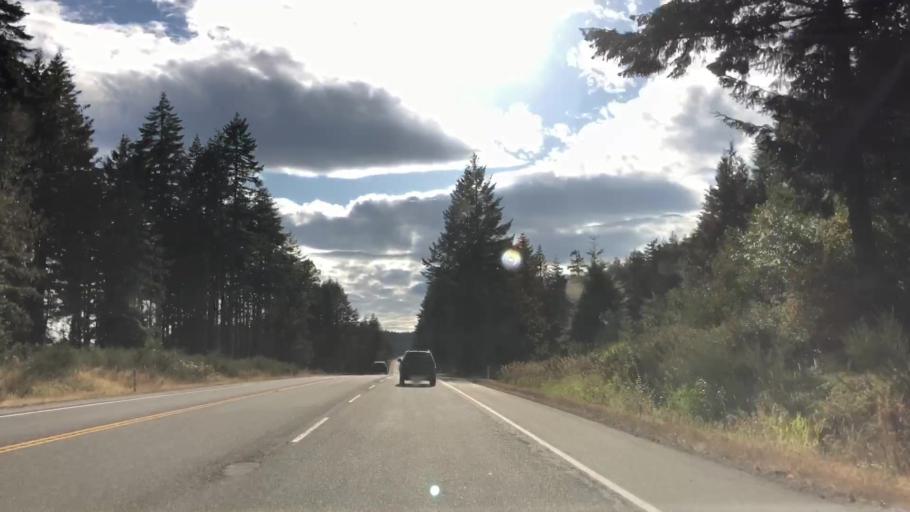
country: CA
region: British Columbia
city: Langford
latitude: 48.5703
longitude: -123.5328
